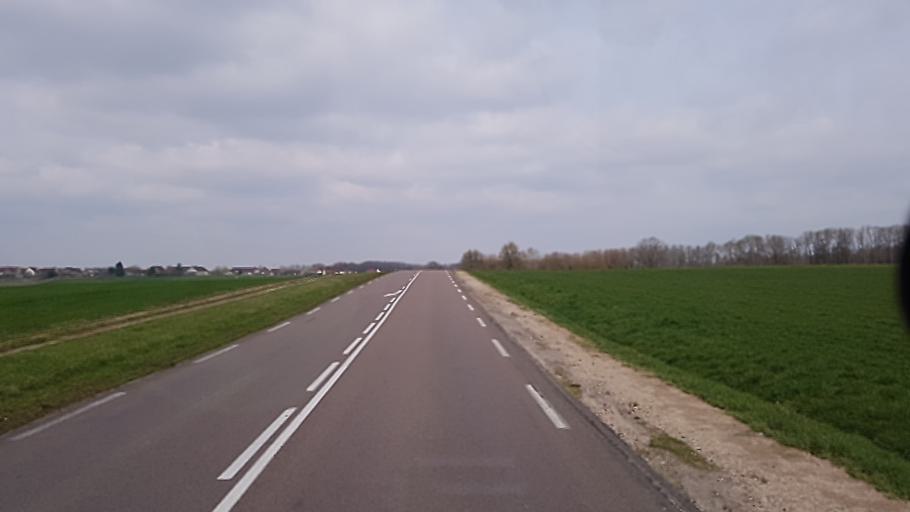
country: FR
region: Bourgogne
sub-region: Departement de la Cote-d'Or
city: Auxonne
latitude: 47.1522
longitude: 5.4163
